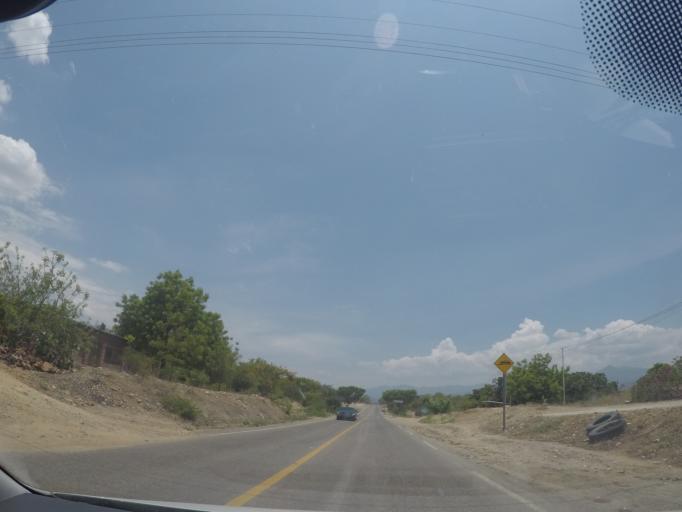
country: MX
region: Oaxaca
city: Santa Maria Jalapa del Marques
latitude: 16.4393
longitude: -95.5074
